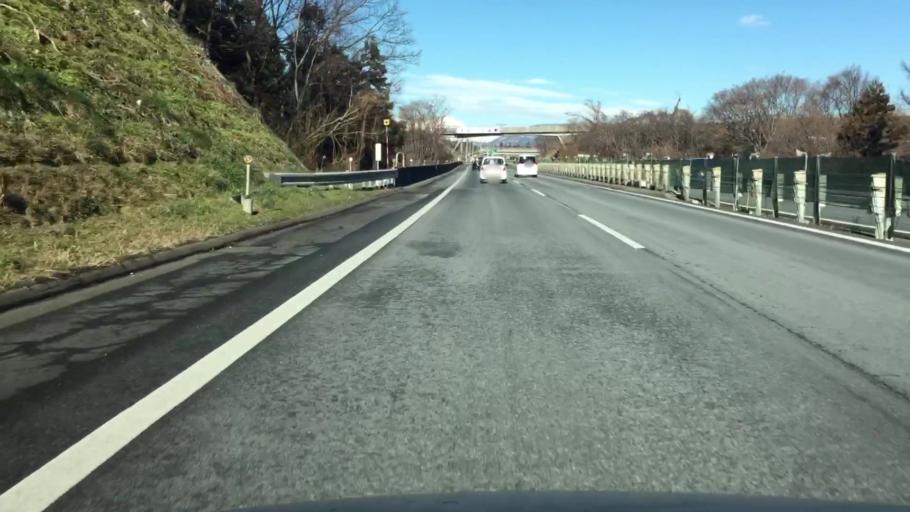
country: JP
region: Gunma
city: Numata
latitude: 36.5951
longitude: 139.0654
